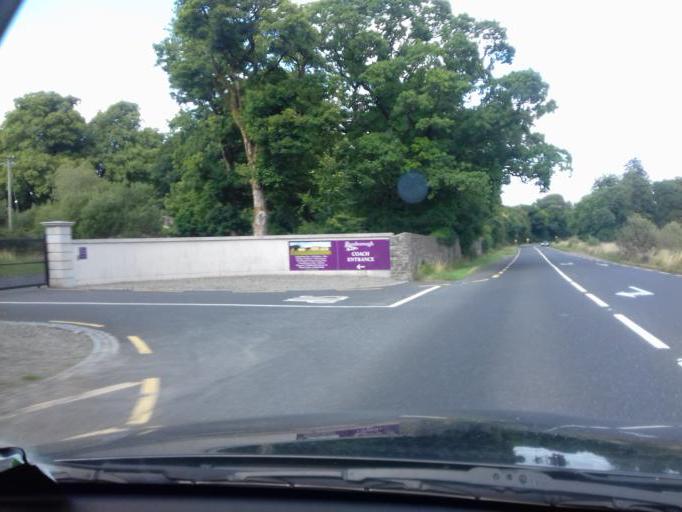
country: IE
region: Leinster
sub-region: Wicklow
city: Valleymount
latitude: 53.1350
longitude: -6.5686
